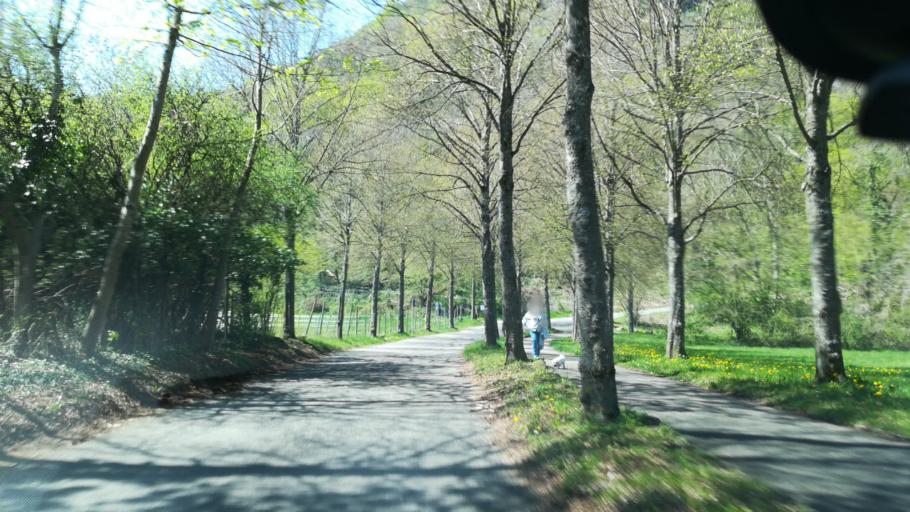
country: DE
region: Baden-Wuerttemberg
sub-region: Freiburg Region
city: Singen
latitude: 47.7628
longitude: 8.8241
